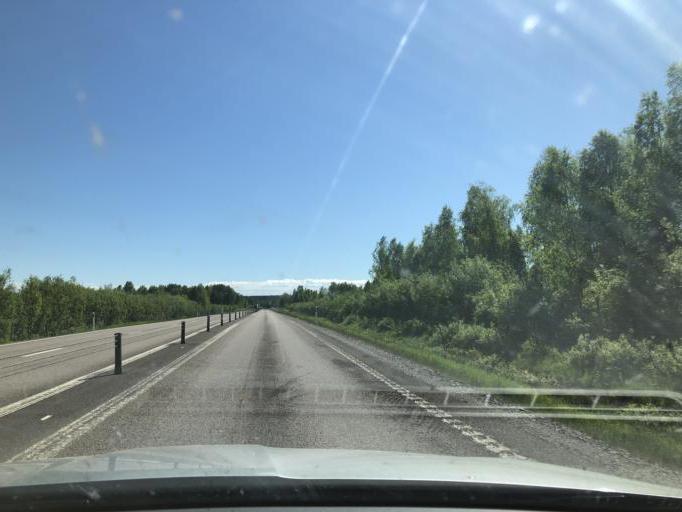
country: SE
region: Norrbotten
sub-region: Kalix Kommun
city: Rolfs
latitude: 65.8922
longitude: 22.9025
